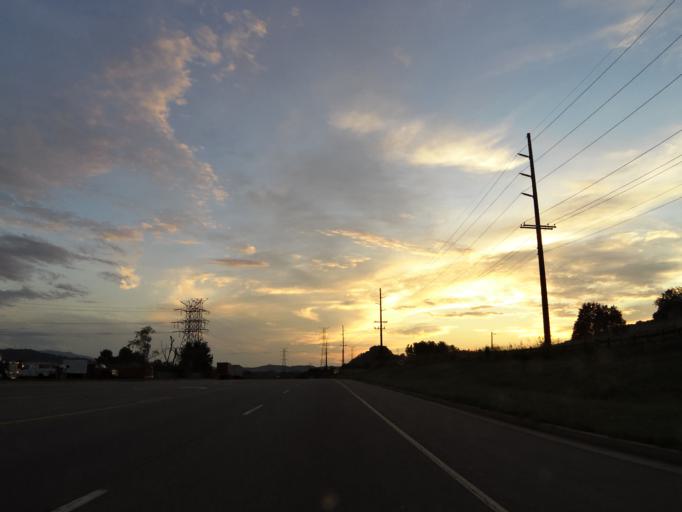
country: US
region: Tennessee
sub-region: Carter County
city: Elizabethton
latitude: 36.3598
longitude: -82.1992
